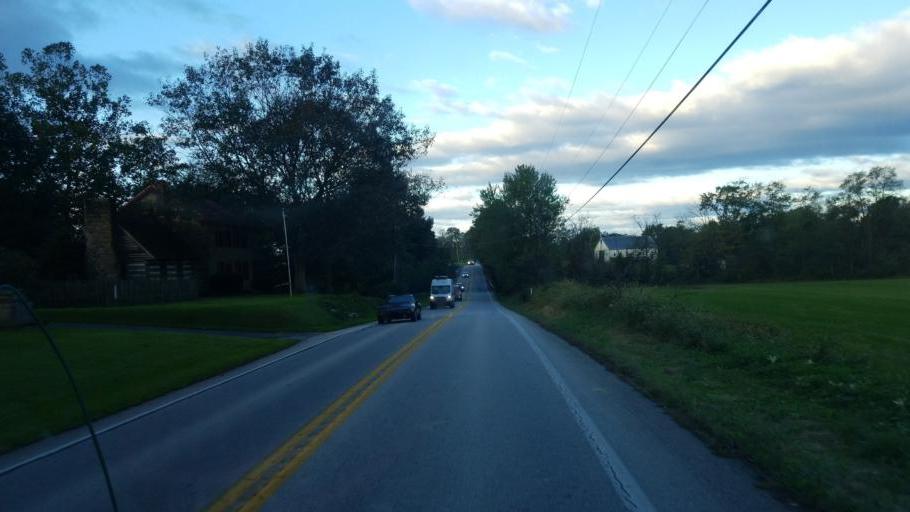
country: US
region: Pennsylvania
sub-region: Adams County
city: East Berlin
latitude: 39.9361
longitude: -76.9310
